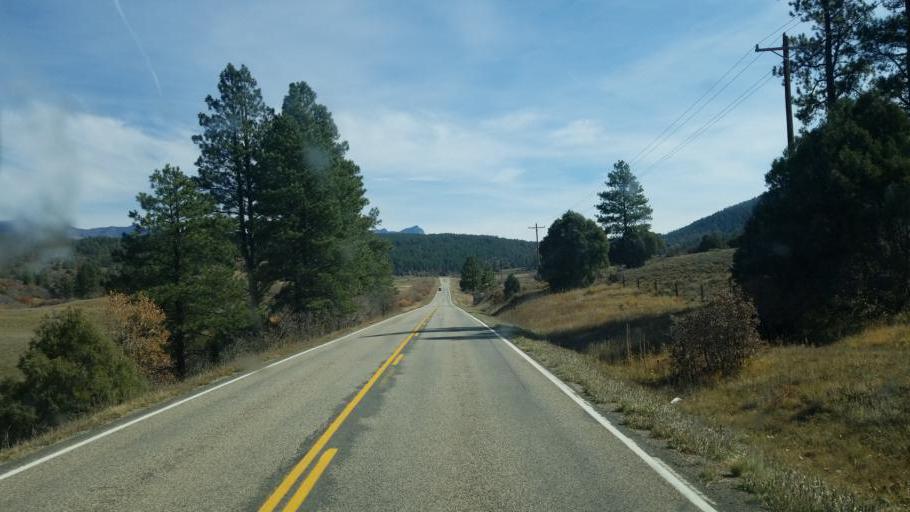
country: US
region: New Mexico
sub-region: Rio Arriba County
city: Dulce
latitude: 37.0802
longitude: -106.8800
